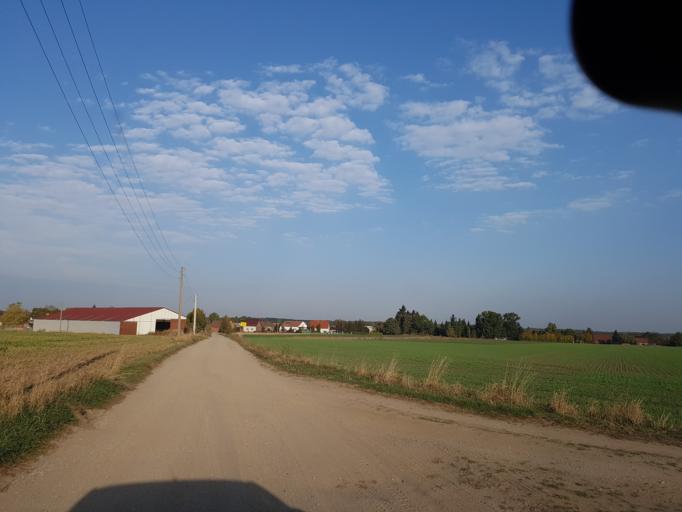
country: DE
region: Brandenburg
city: Finsterwalde
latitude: 51.6015
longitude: 13.6761
